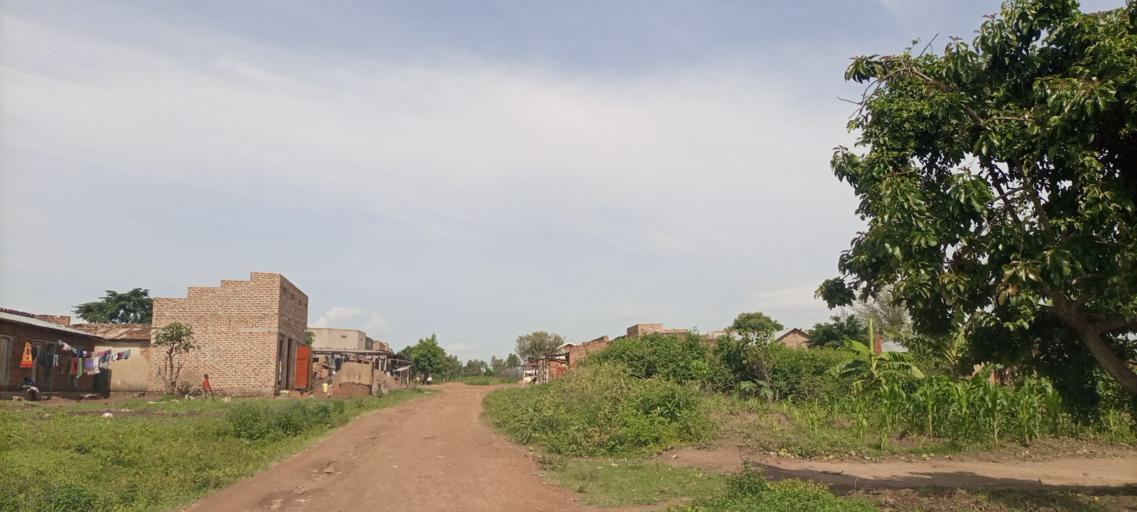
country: UG
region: Eastern Region
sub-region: Mbale District
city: Mbale
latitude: 1.1308
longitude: 34.0460
